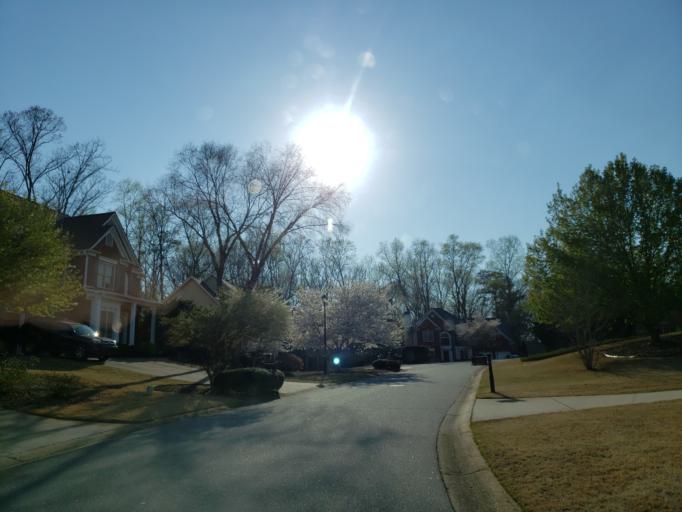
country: US
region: Georgia
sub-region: Cobb County
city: Marietta
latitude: 33.9806
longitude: -84.5148
